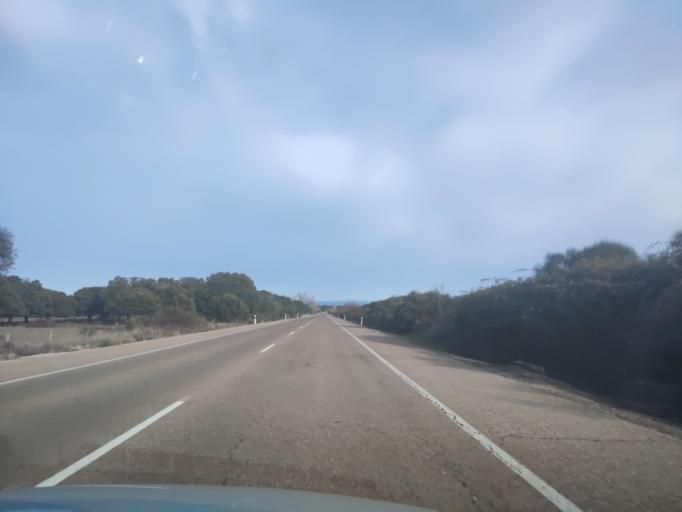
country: ES
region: Castille and Leon
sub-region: Provincia de Salamanca
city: Espeja
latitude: 40.5900
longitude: -6.7264
